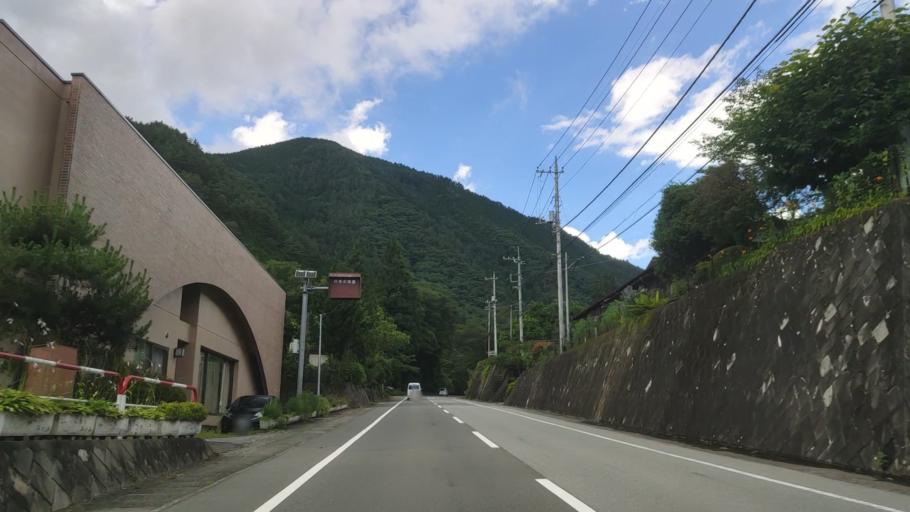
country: JP
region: Yamanashi
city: Enzan
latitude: 35.7933
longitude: 138.7391
